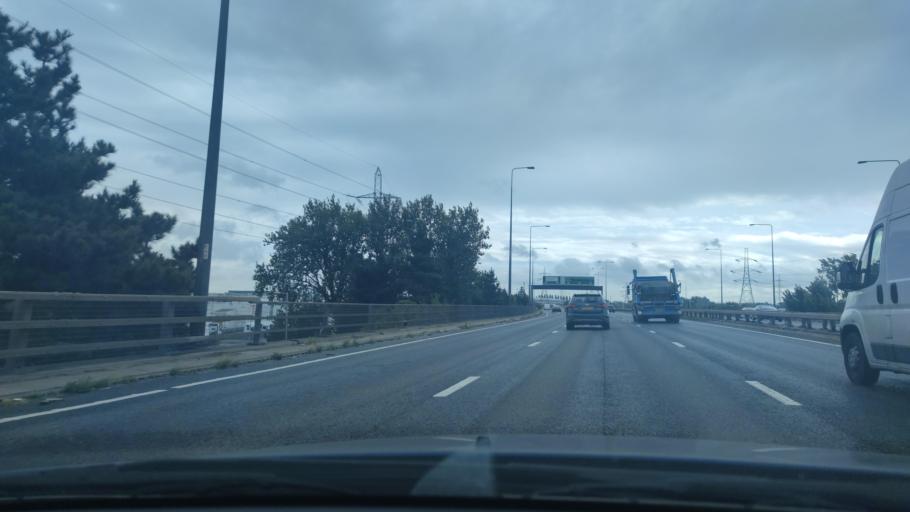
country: GB
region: England
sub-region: Greater London
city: Dagenham
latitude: 51.5216
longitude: 0.1611
